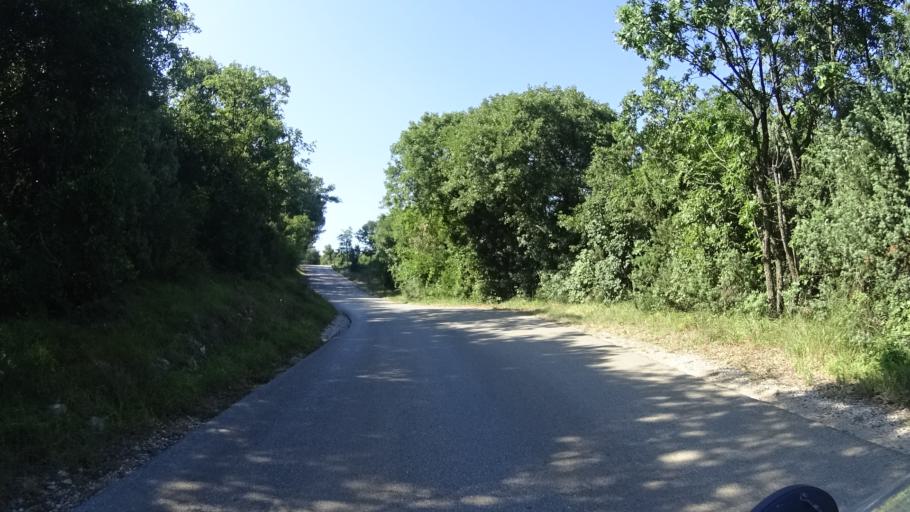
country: HR
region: Istarska
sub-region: Grad Labin
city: Rabac
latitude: 45.0074
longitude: 14.1618
